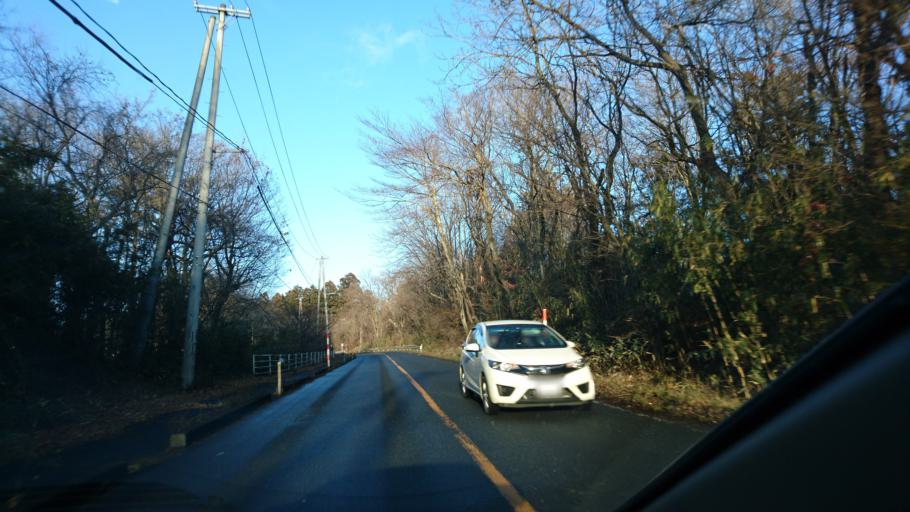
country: JP
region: Miyagi
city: Furukawa
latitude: 38.6133
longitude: 140.8719
